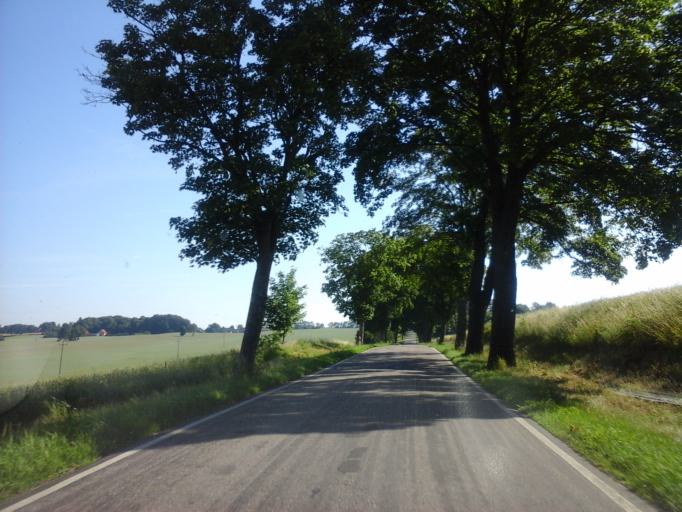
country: PL
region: West Pomeranian Voivodeship
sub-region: Powiat drawski
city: Drawsko Pomorskie
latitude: 53.5909
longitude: 15.8925
